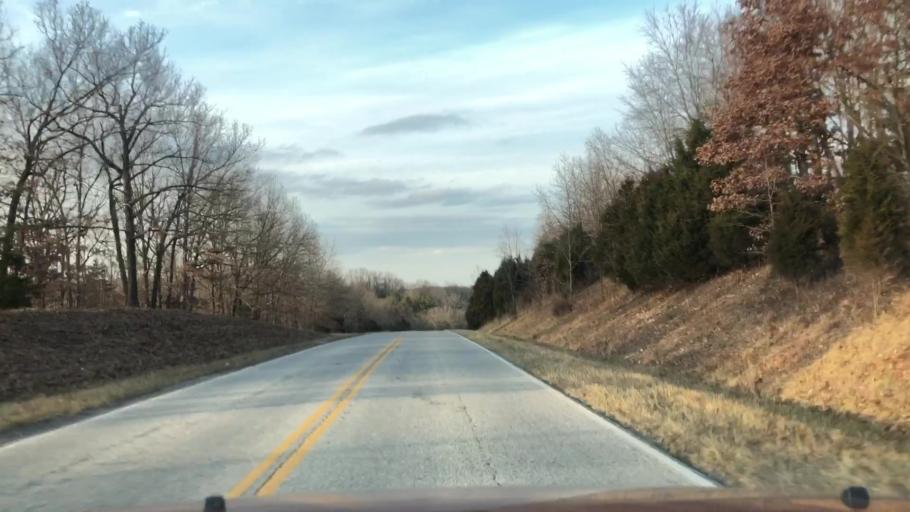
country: US
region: Missouri
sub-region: Webster County
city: Marshfield
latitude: 37.2370
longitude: -92.8793
